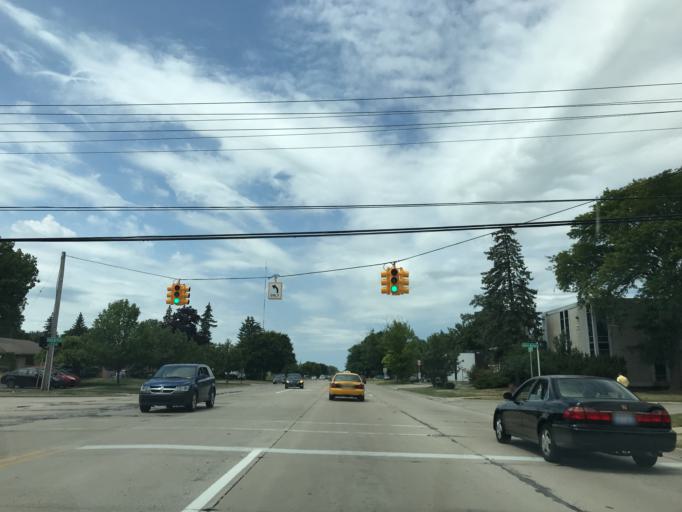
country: US
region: Michigan
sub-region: Oakland County
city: Southfield
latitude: 42.4732
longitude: -83.2306
